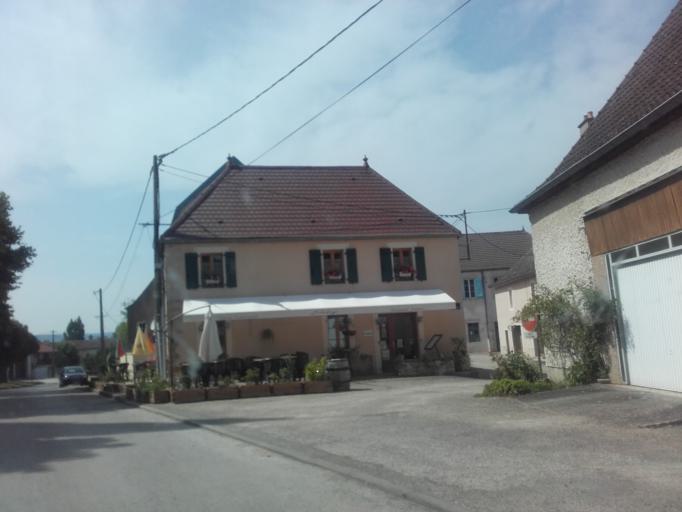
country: FR
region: Bourgogne
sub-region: Departement de Saone-et-Loire
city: Demigny
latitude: 46.9311
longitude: 4.8374
